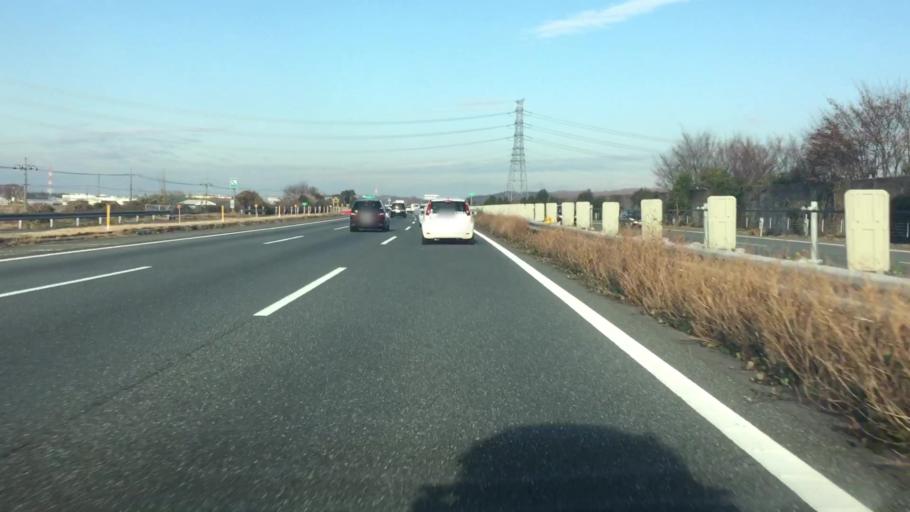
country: JP
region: Saitama
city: Honjo
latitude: 36.1998
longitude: 139.1828
